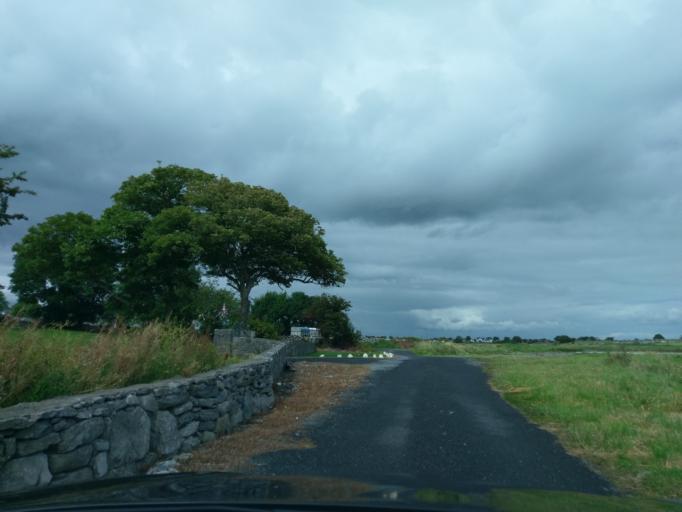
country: IE
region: Connaught
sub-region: County Galway
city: Oranmore
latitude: 53.2123
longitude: -8.9354
